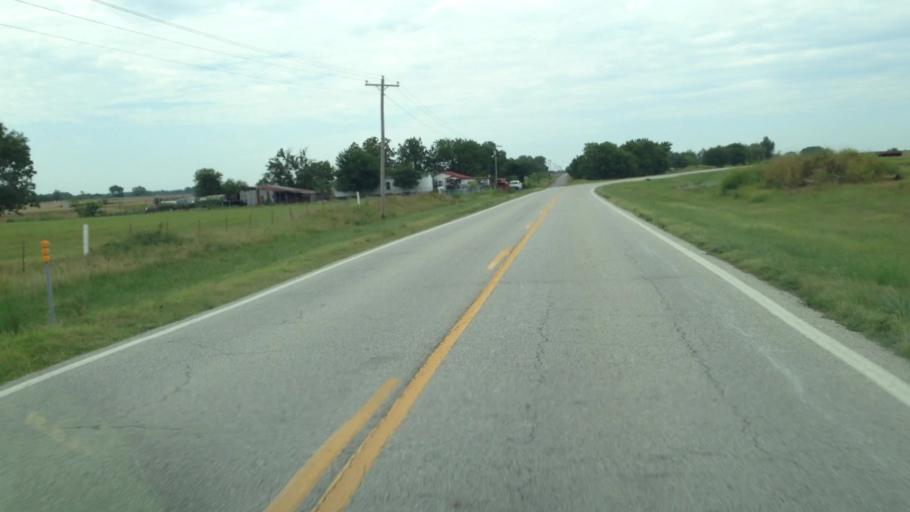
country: US
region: Oklahoma
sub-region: Craig County
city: Vinita
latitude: 36.8177
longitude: -95.1436
